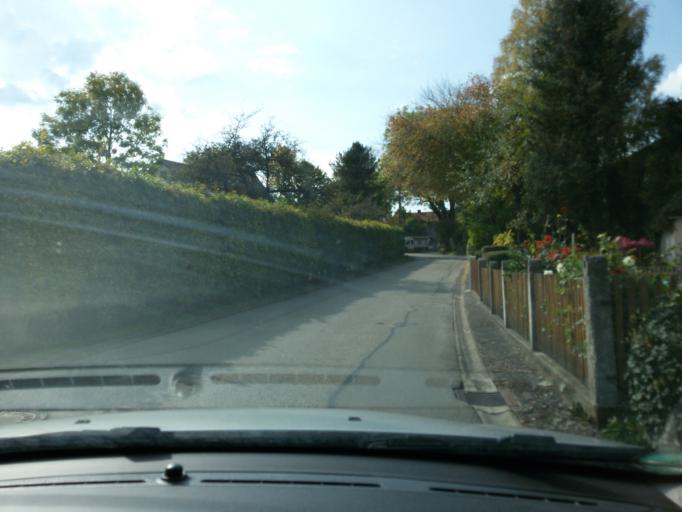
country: DE
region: Bavaria
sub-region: Upper Bavaria
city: Hurlach
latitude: 48.0718
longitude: 10.8051
